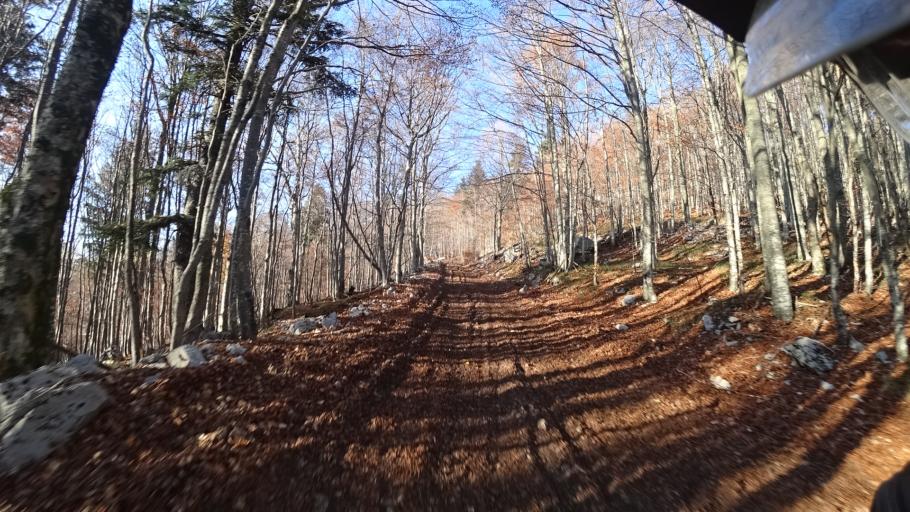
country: HR
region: Primorsko-Goranska
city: Klana
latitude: 45.4800
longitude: 14.4486
